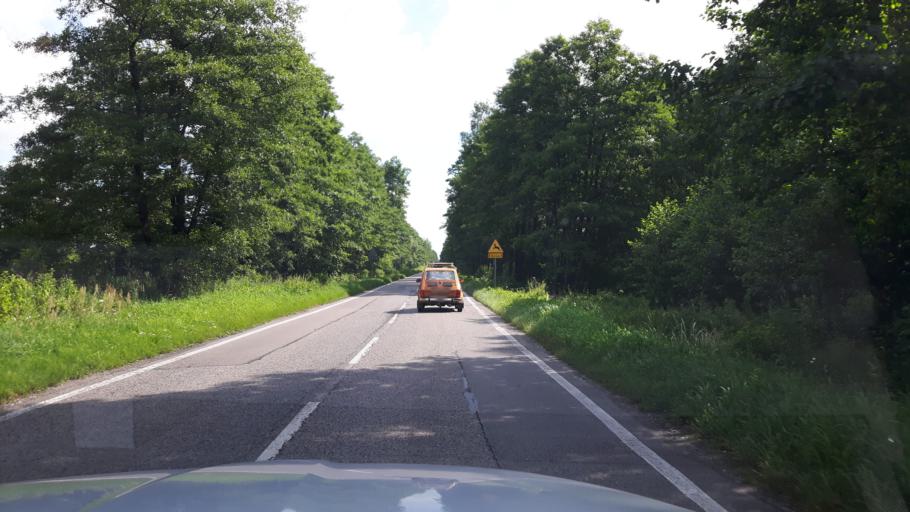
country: PL
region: Masovian Voivodeship
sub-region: Powiat wolominski
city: Tluszcz
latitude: 52.4173
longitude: 21.5084
